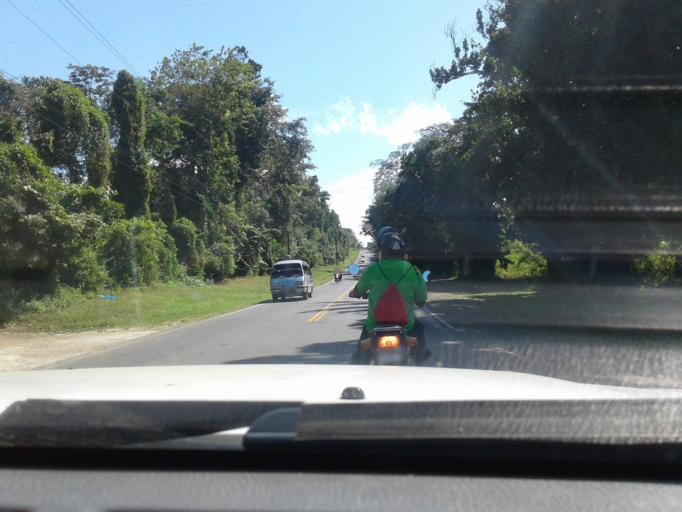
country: NI
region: Carazo
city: La Paz de Oriente
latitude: 11.8247
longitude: -86.1642
